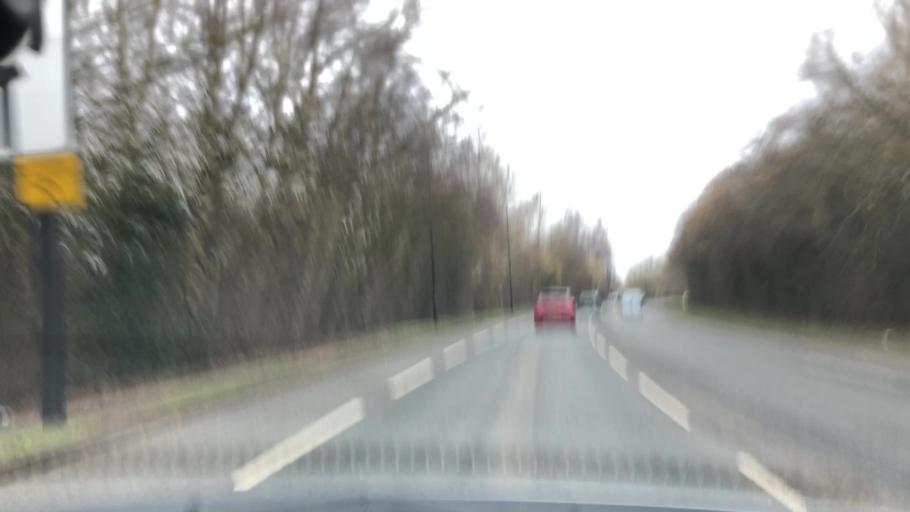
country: GB
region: England
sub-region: Coventry
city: Keresley
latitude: 52.4331
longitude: -1.5534
